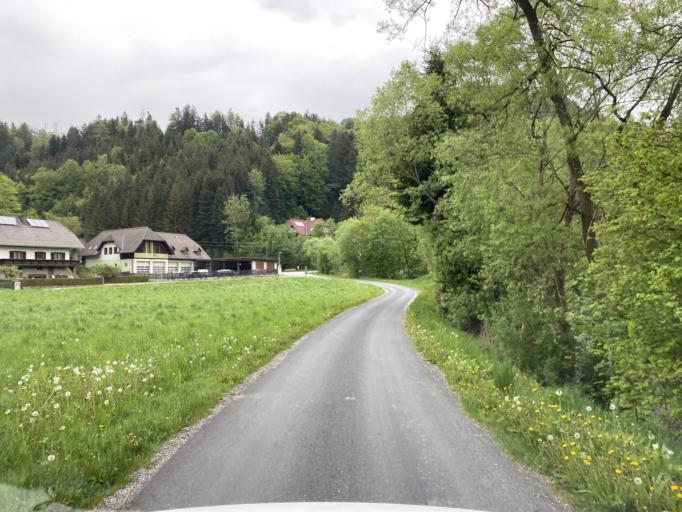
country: AT
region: Styria
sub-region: Politischer Bezirk Weiz
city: Koglhof
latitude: 47.3137
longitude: 15.6865
